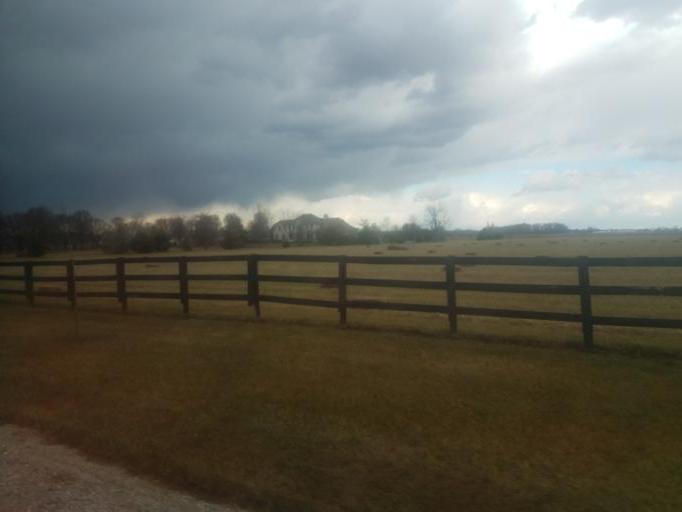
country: US
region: Ohio
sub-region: Marion County
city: Prospect
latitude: 40.4545
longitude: -83.1124
